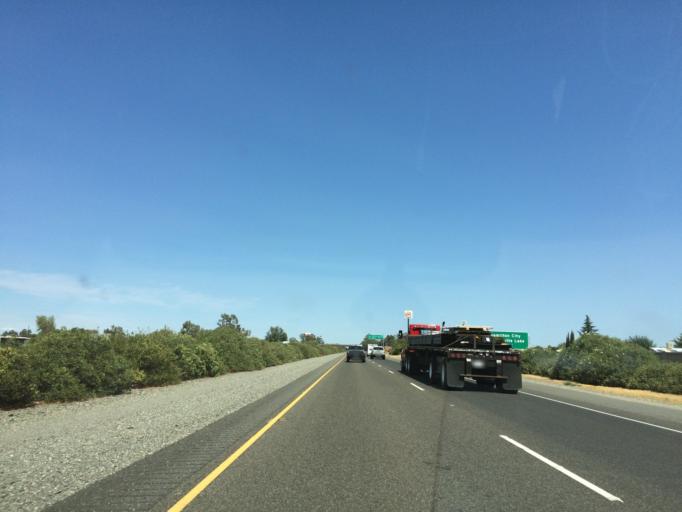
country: US
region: California
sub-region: Glenn County
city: Orland
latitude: 39.7444
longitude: -122.2055
